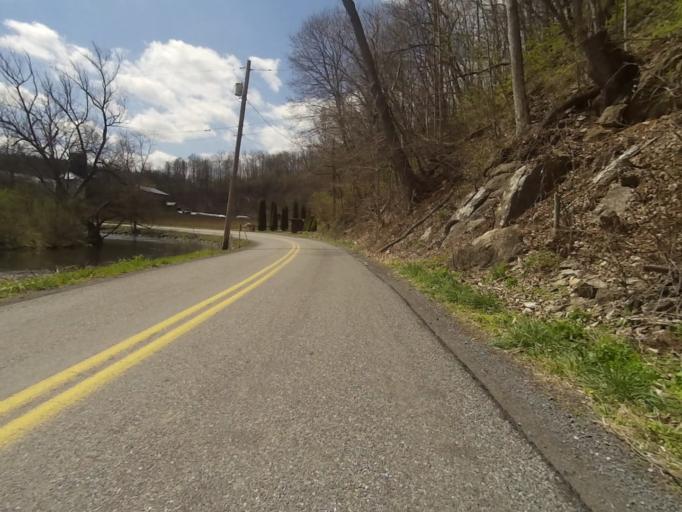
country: US
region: Pennsylvania
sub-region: Centre County
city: Bellefonte
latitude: 40.8912
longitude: -77.7950
